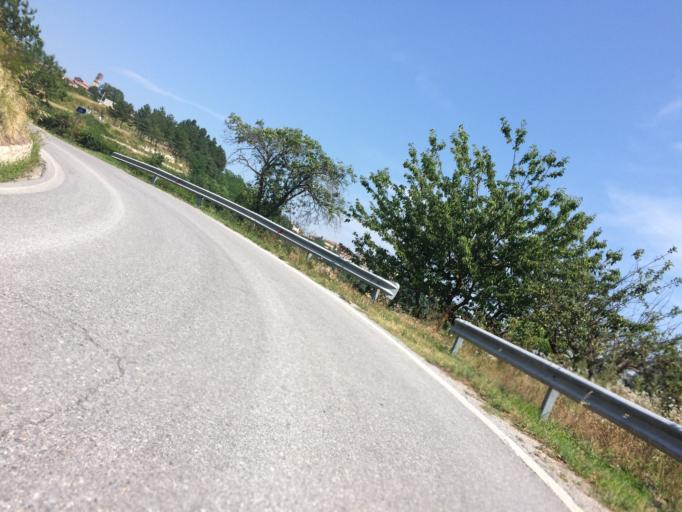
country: IT
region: Piedmont
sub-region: Provincia di Cuneo
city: Serravalle Langhe
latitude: 44.5583
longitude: 8.0499
